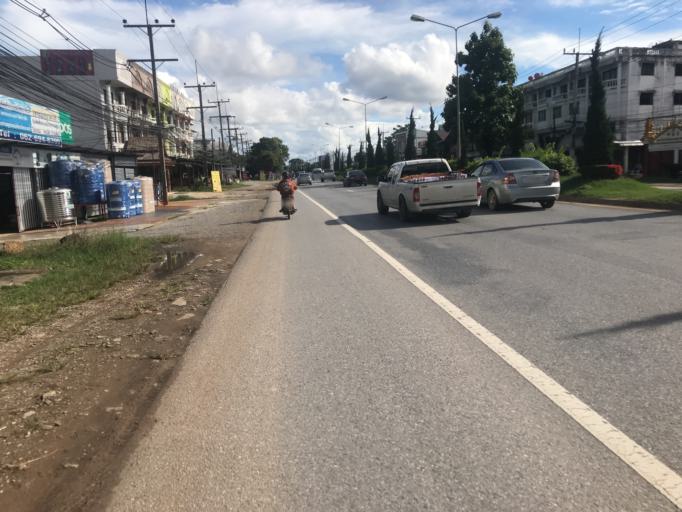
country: TH
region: Chiang Rai
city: Chiang Rai
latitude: 19.9553
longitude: 99.8511
